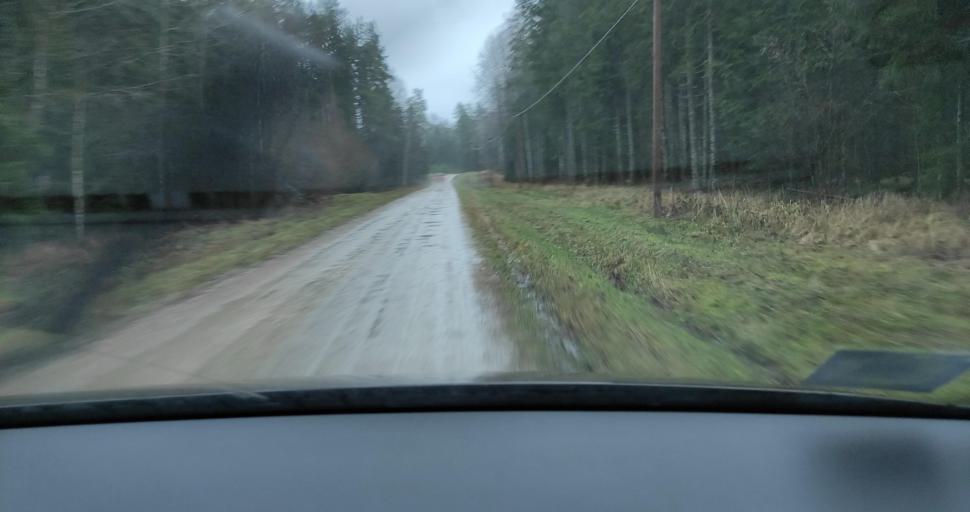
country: LV
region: Skrunda
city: Skrunda
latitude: 56.6117
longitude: 22.1739
